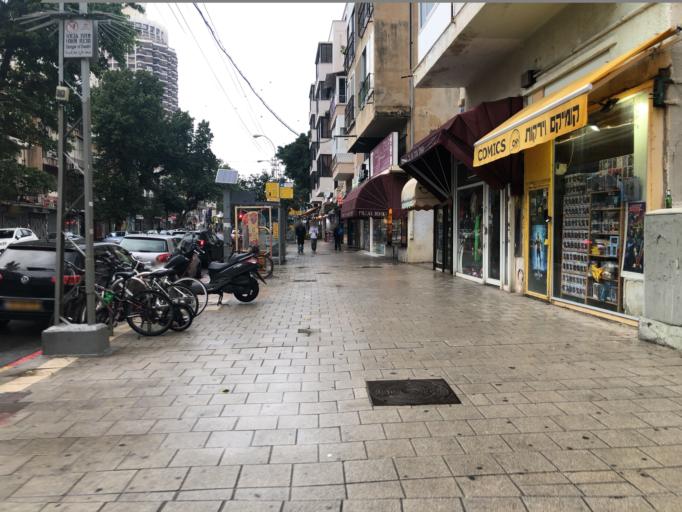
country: IL
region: Tel Aviv
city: Tel Aviv
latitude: 32.0730
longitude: 34.7748
